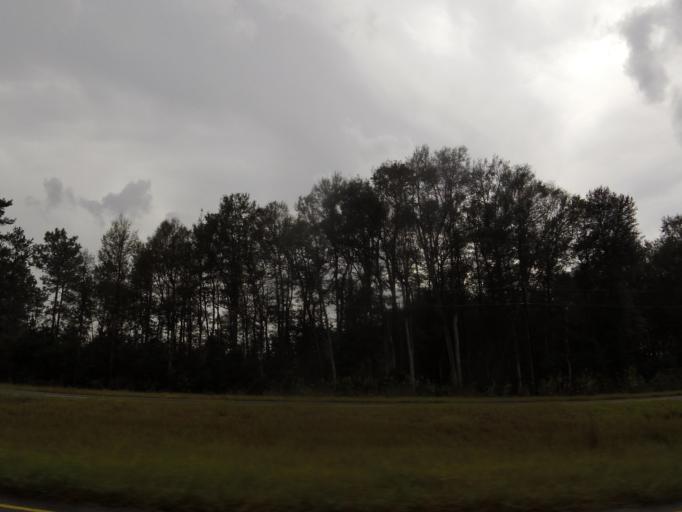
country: US
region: Georgia
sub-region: Wayne County
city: Jesup
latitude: 31.4850
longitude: -81.7373
